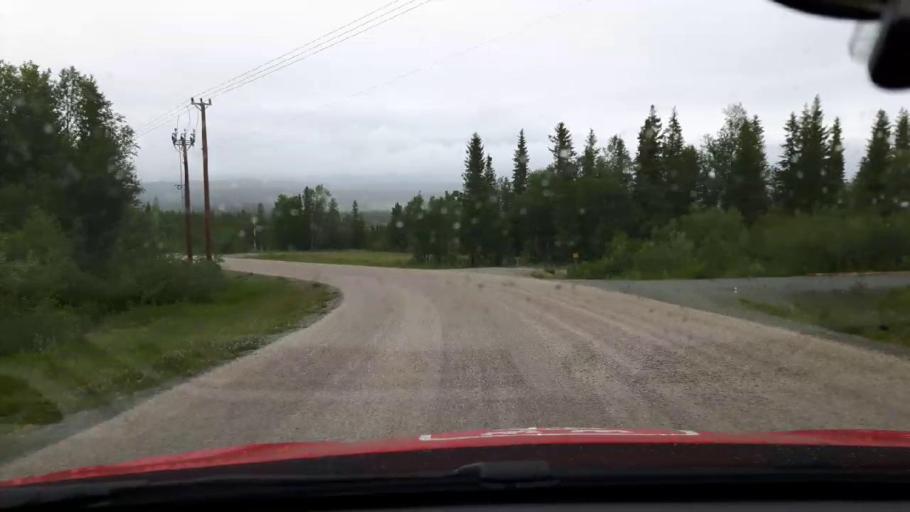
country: SE
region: Jaemtland
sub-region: Are Kommun
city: Are
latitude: 63.2565
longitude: 12.4273
